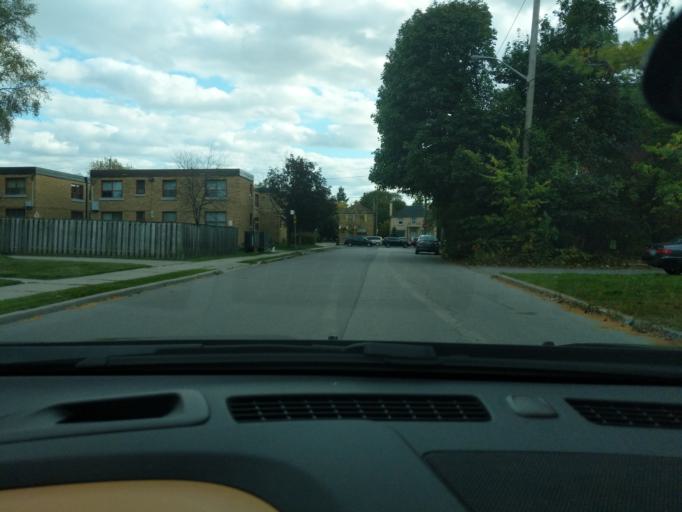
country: CA
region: Ontario
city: Toronto
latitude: 43.7189
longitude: -79.4354
